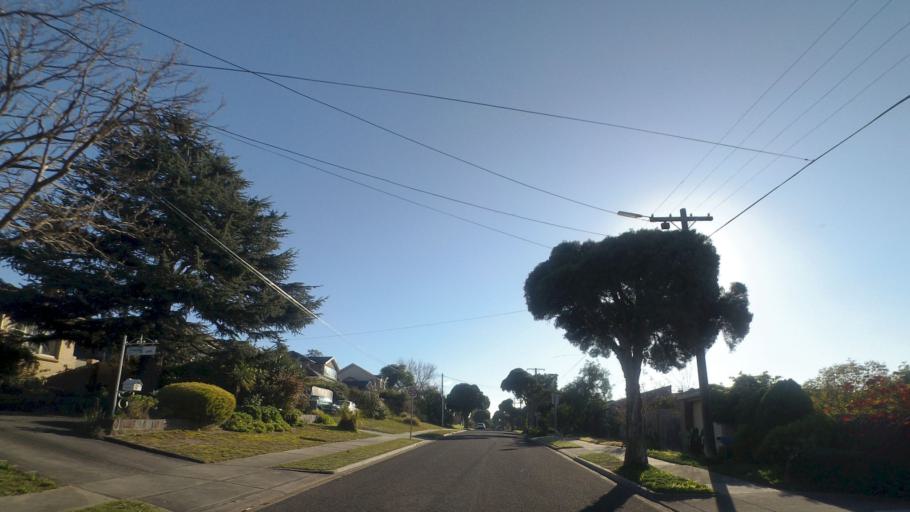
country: AU
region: Victoria
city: Macleod
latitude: -37.7340
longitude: 145.0628
